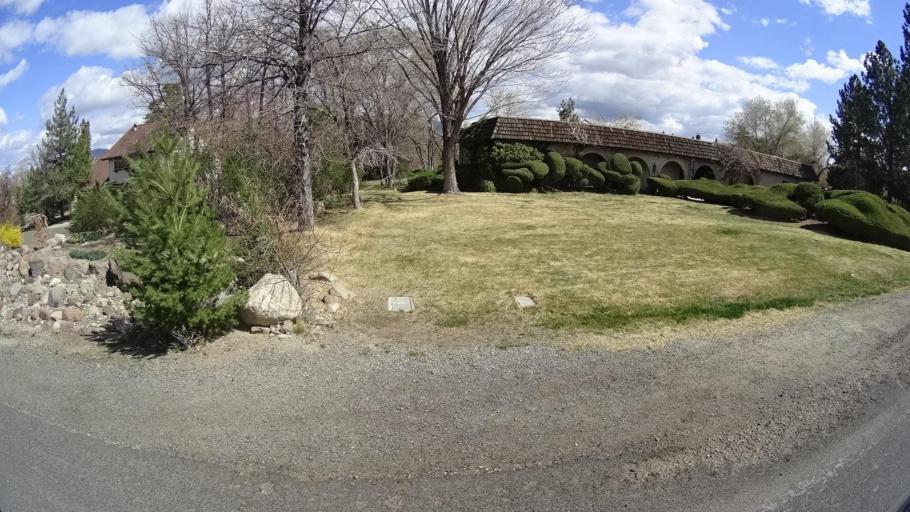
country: US
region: Nevada
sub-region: Washoe County
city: Reno
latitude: 39.4241
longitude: -119.7784
